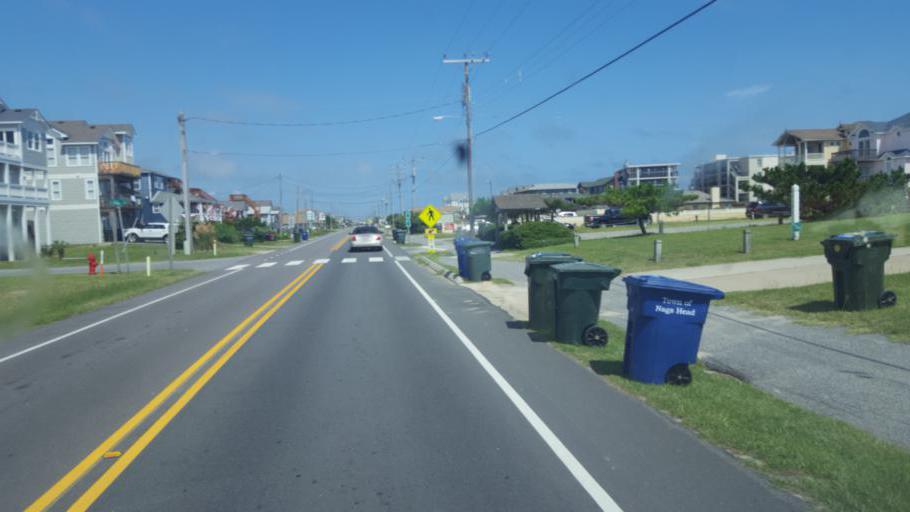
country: US
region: North Carolina
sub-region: Dare County
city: Nags Head
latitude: 35.9128
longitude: -75.5991
